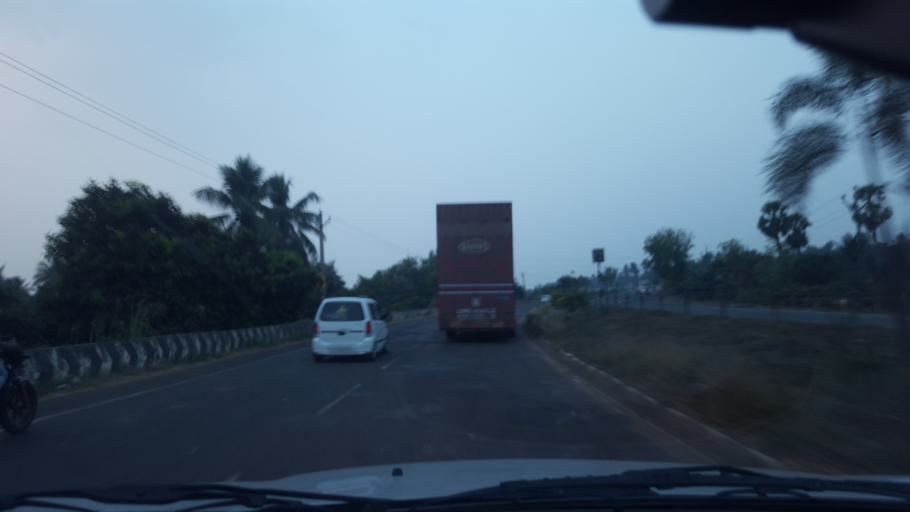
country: IN
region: Andhra Pradesh
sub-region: East Godavari
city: Rajahmundry
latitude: 16.9131
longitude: 81.7929
